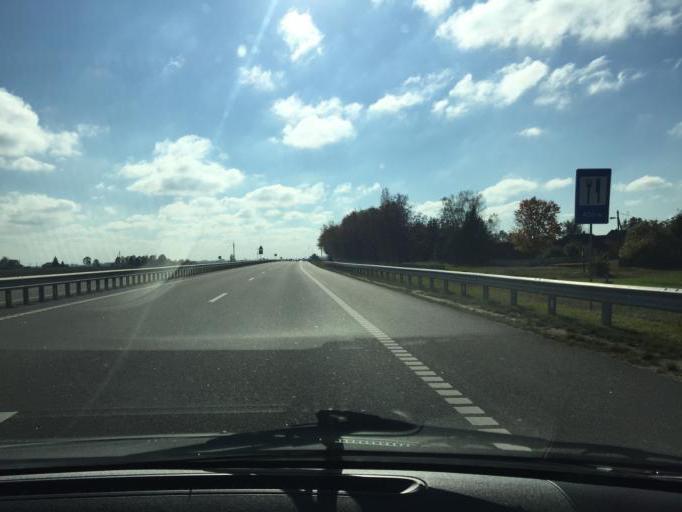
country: BY
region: Minsk
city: Slutsk
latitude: 53.1546
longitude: 27.5518
